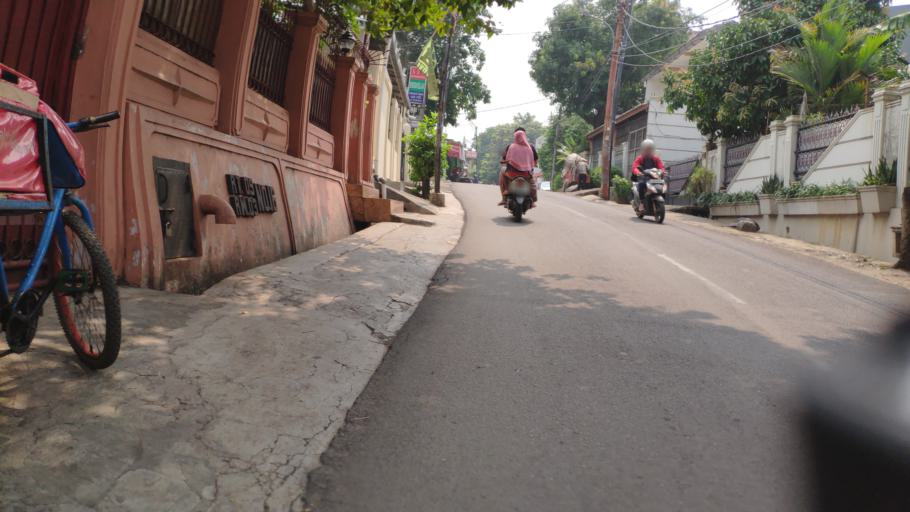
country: ID
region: West Java
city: Depok
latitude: -6.3266
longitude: 106.8241
